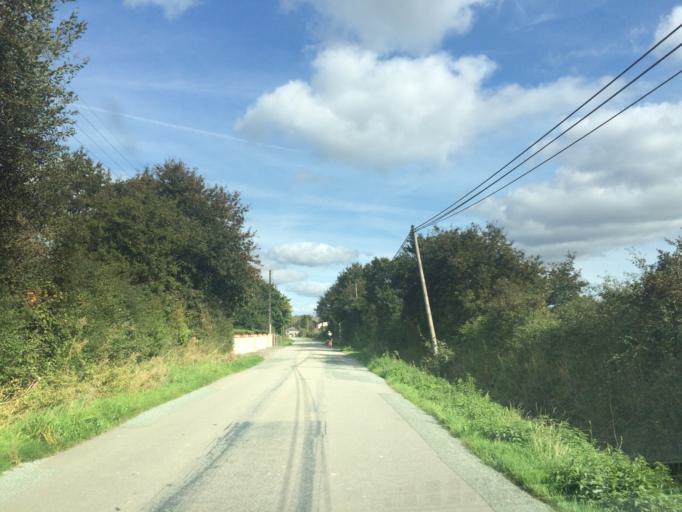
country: FR
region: Pays de la Loire
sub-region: Departement de la Loire-Atlantique
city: Chemere
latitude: 47.0989
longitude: -1.9143
